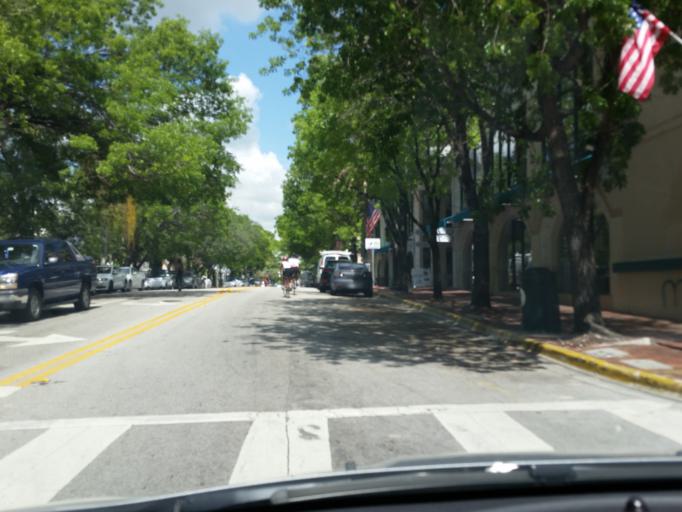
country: US
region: Florida
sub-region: Miami-Dade County
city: Coconut Grove
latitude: 25.7283
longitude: -80.2395
